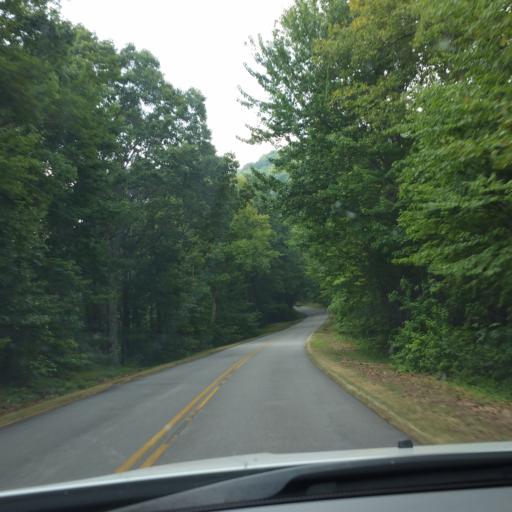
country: US
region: North Carolina
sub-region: Buncombe County
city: Avery Creek
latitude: 35.4584
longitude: -82.6375
